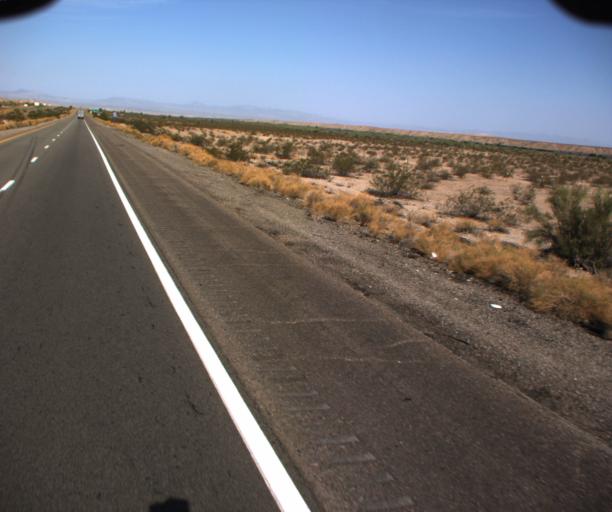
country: US
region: Arizona
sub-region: Mohave County
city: Desert Hills
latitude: 34.7295
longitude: -114.3246
